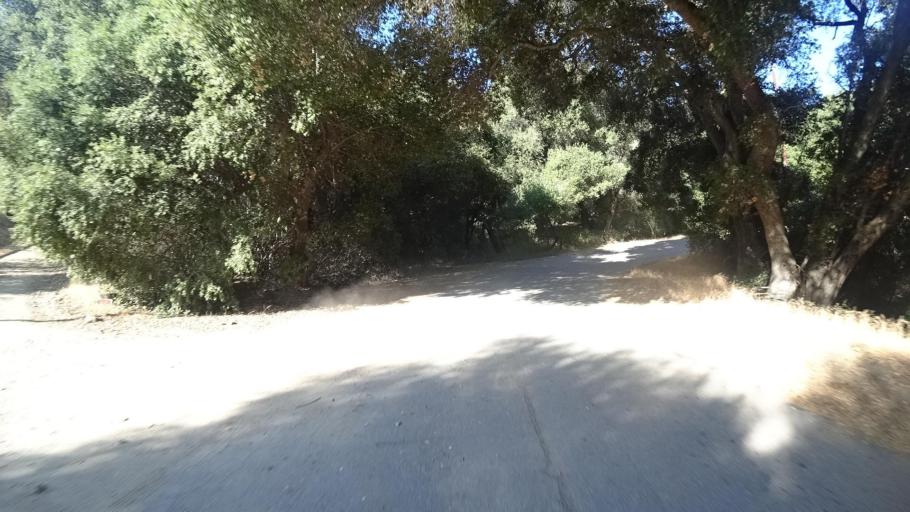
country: US
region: California
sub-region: San Diego County
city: Julian
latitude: 33.2163
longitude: -116.7451
